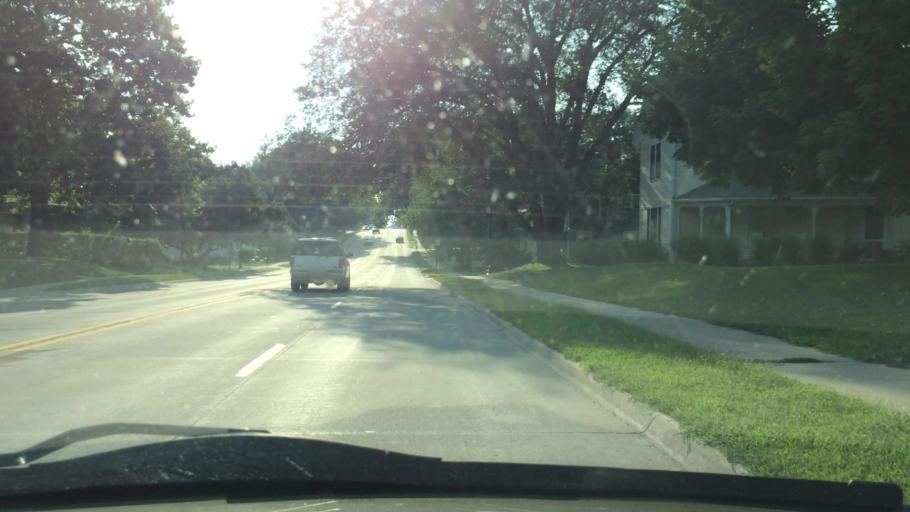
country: US
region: Iowa
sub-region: Henry County
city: Mount Pleasant
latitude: 40.9647
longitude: -91.5462
